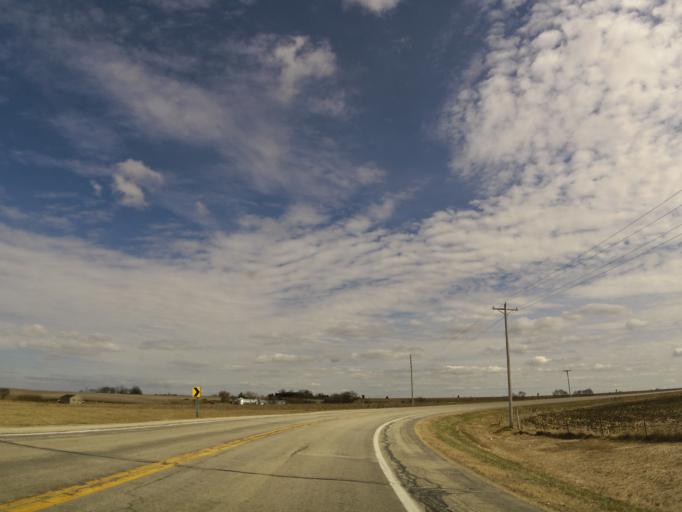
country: US
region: Minnesota
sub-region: Olmsted County
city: Rochester
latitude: 43.9454
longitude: -92.4097
